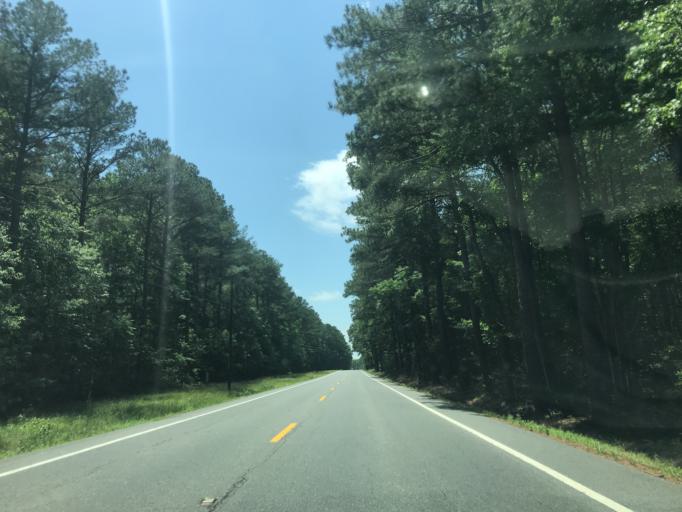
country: US
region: Maryland
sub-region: Dorchester County
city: Hurlock
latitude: 38.6333
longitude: -75.7935
